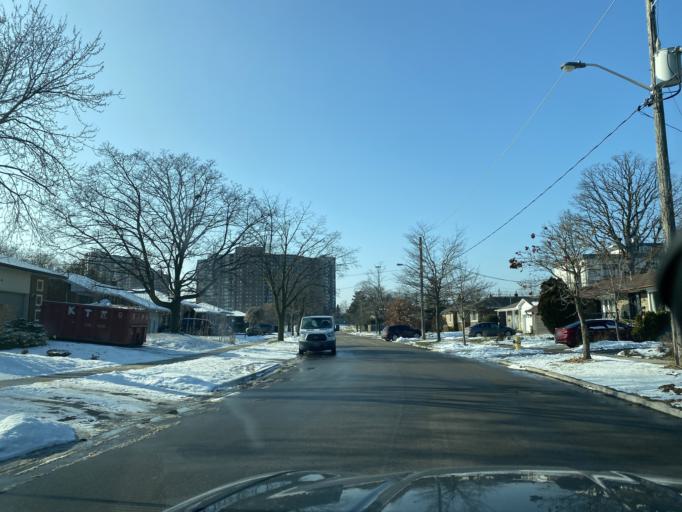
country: CA
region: Ontario
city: Etobicoke
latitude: 43.6581
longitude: -79.5657
